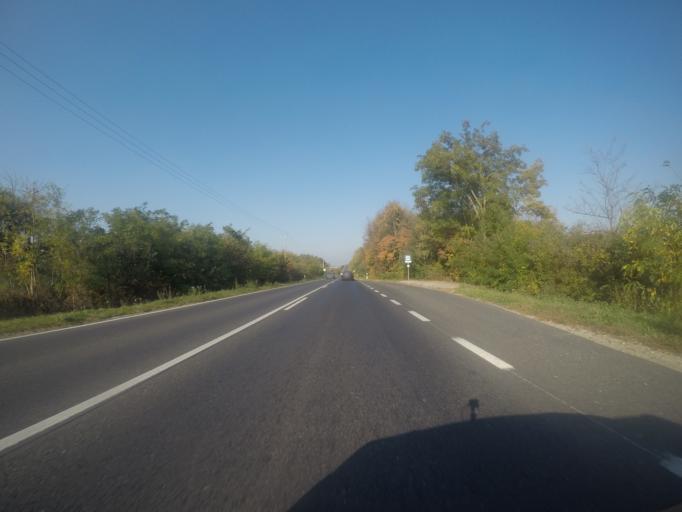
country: HU
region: Fejer
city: Baracs
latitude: 46.8508
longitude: 18.9120
